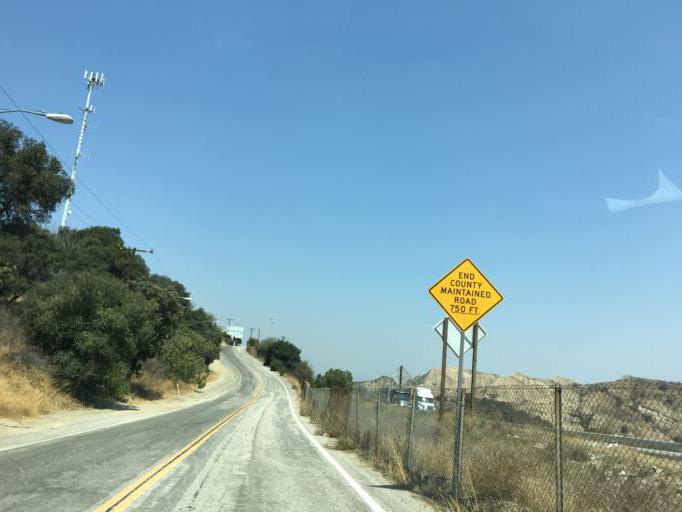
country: US
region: California
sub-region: Los Angeles County
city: Santa Clarita
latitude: 34.3428
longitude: -118.5298
